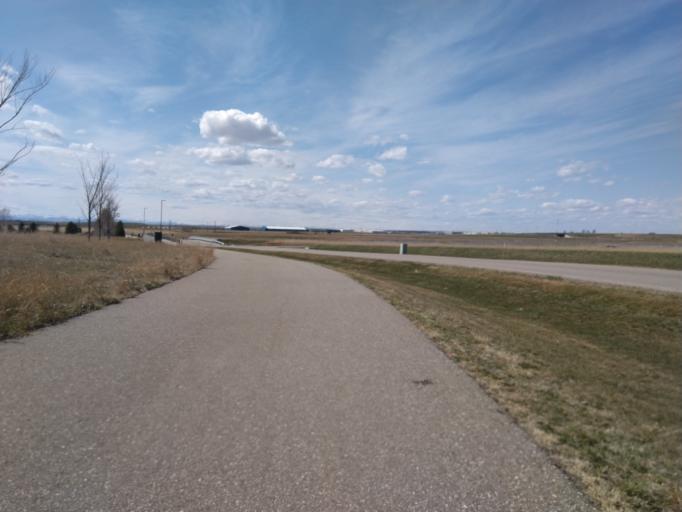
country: CA
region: Alberta
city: Chestermere
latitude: 50.9389
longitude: -113.9062
